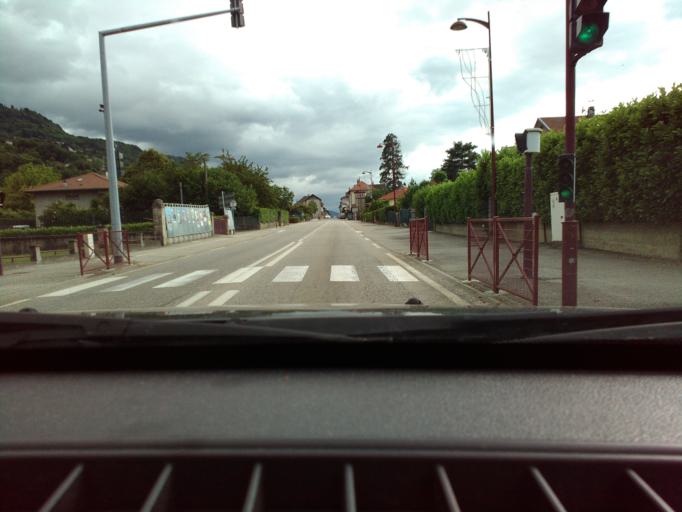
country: FR
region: Rhone-Alpes
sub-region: Departement de l'Isere
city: Froges
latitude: 45.2766
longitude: 5.9276
